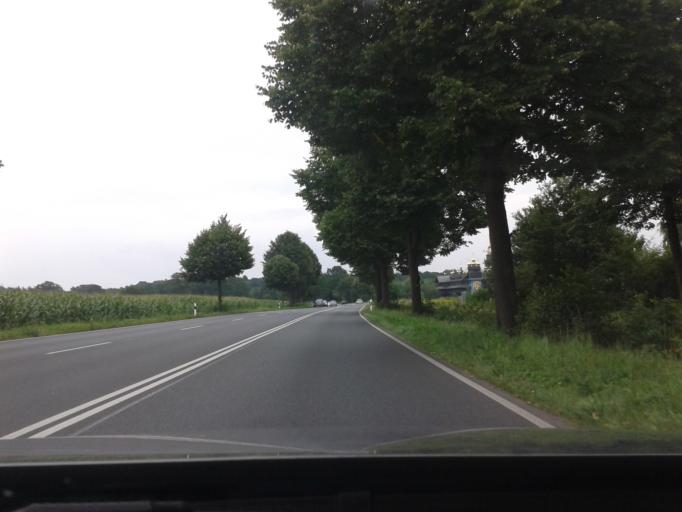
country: DE
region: Lower Saxony
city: Gifhorn
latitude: 52.4946
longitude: 10.5508
